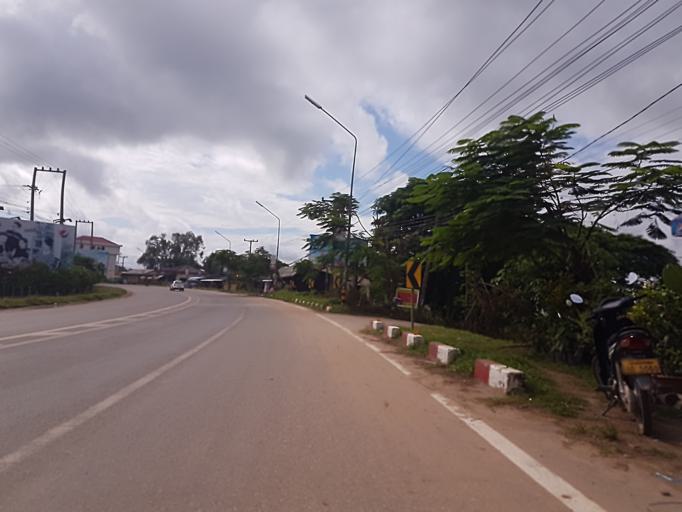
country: TH
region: Nong Khai
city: Tha Bo
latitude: 17.8718
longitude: 102.6533
